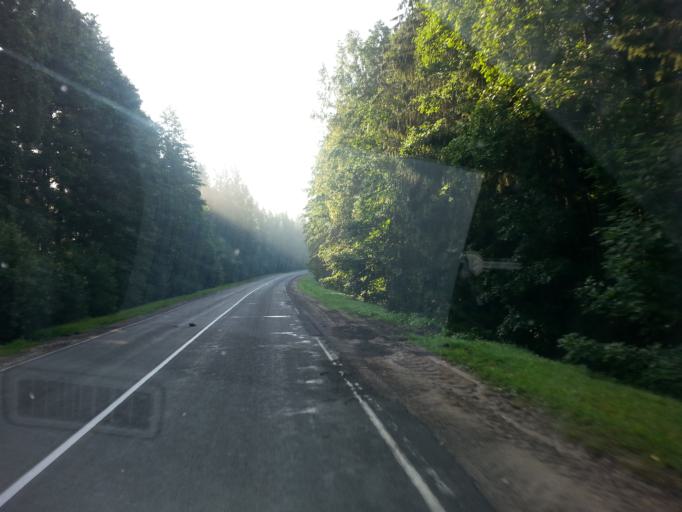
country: BY
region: Minsk
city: Myadzyel
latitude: 54.7663
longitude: 27.0919
